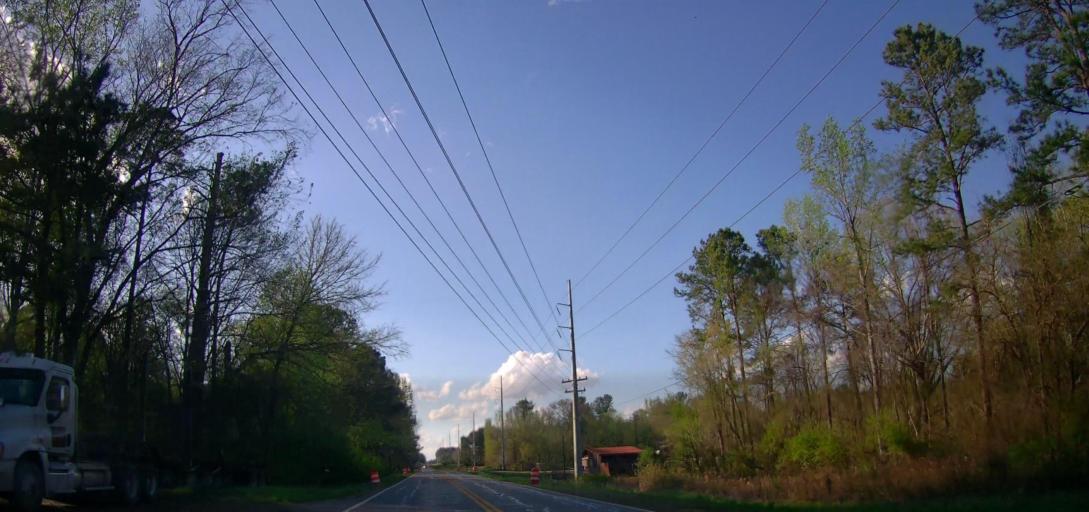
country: US
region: Georgia
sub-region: Baldwin County
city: Milledgeville
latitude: 33.1484
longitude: -83.3409
